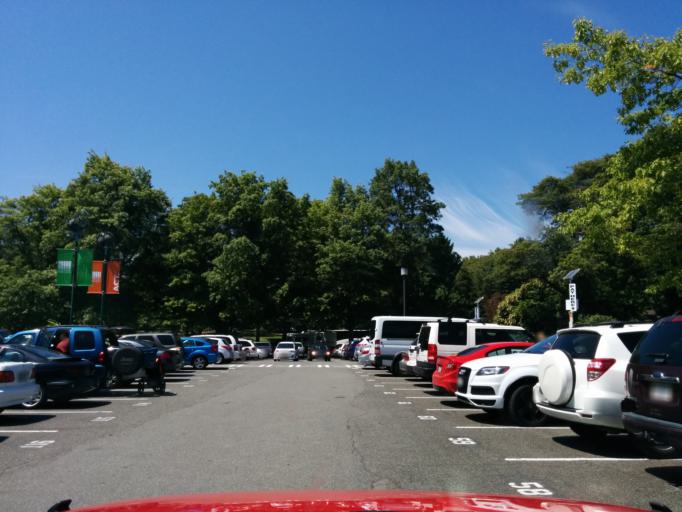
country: US
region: Washington
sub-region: King County
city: Seattle
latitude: 47.6658
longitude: -122.3505
